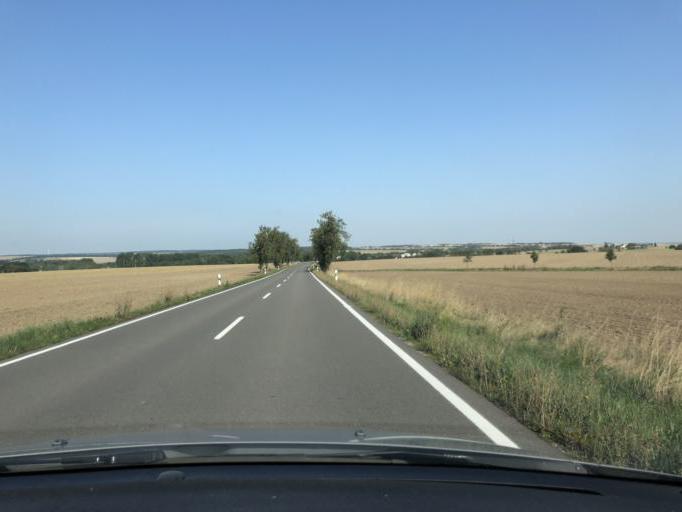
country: DE
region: Thuringia
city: Rastenberg
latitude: 51.1899
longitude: 11.4907
